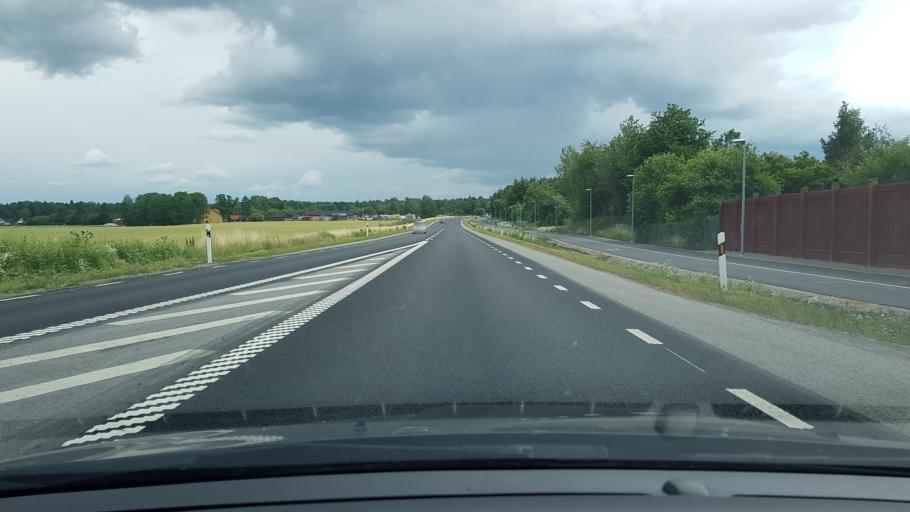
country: SE
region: Uppsala
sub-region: Uppsala Kommun
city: Saevja
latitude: 59.8274
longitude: 17.6952
